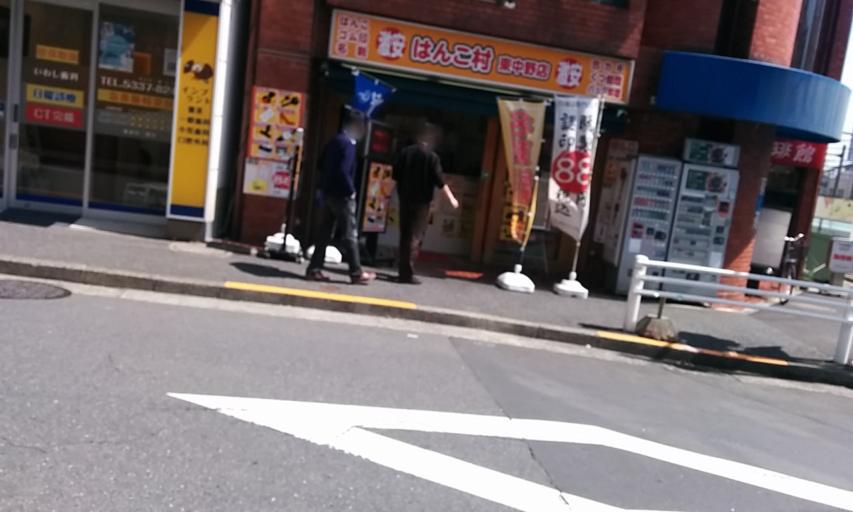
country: JP
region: Tokyo
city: Tokyo
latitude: 35.7066
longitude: 139.6863
